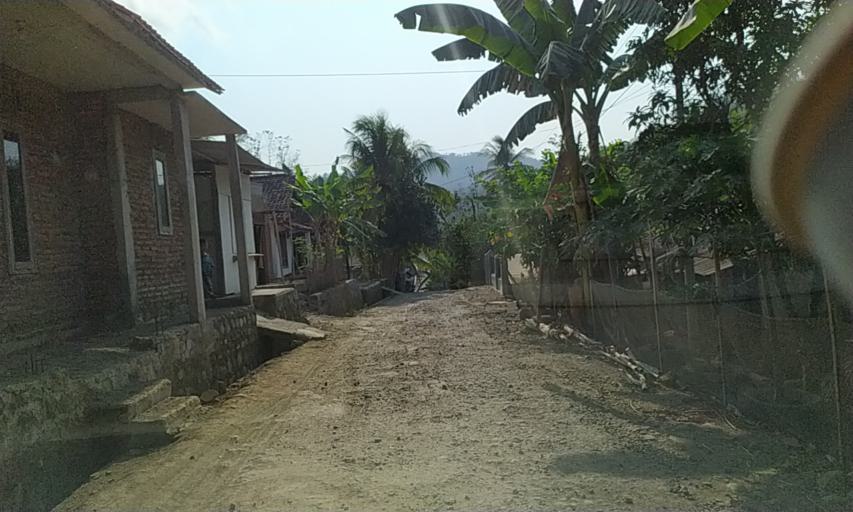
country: ID
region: Central Java
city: Jambuluwuk
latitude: -7.3239
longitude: 108.8755
